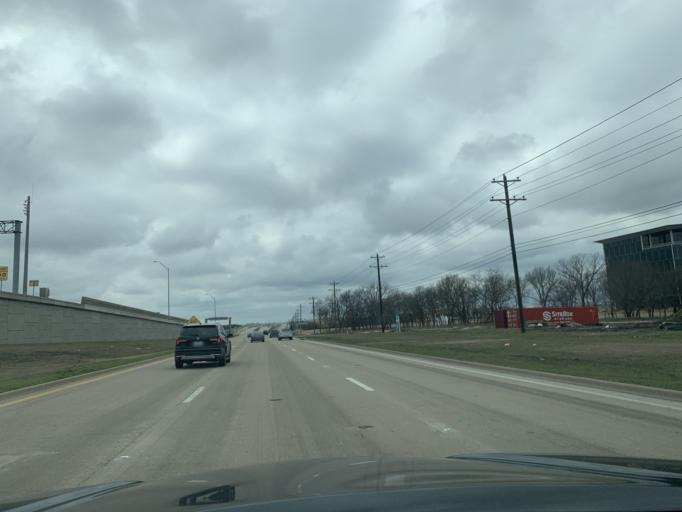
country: US
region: Texas
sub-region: Collin County
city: Allen
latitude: 33.1339
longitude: -96.7096
